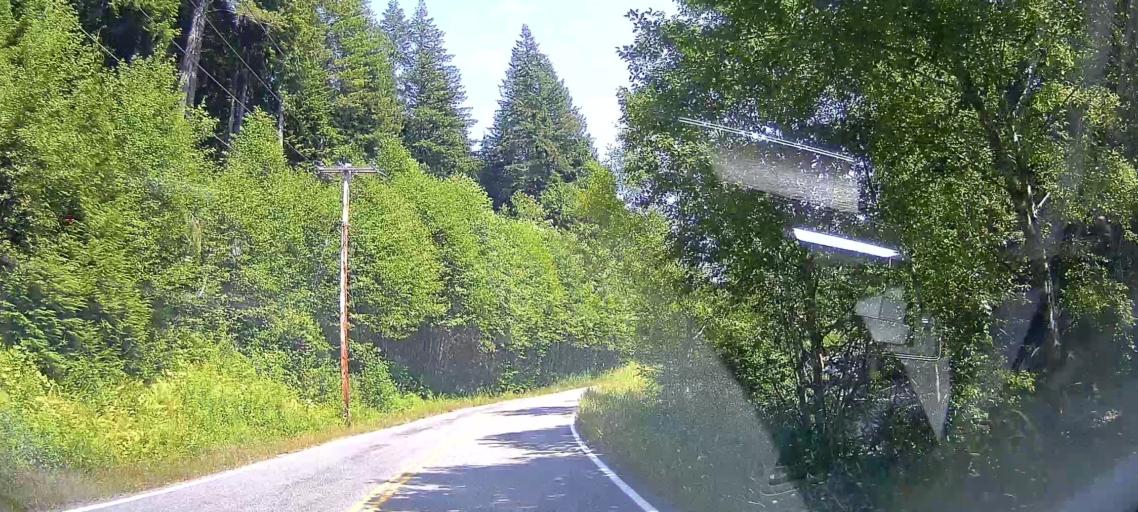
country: US
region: Washington
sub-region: Snohomish County
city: Bryant
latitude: 48.3431
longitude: -122.0879
